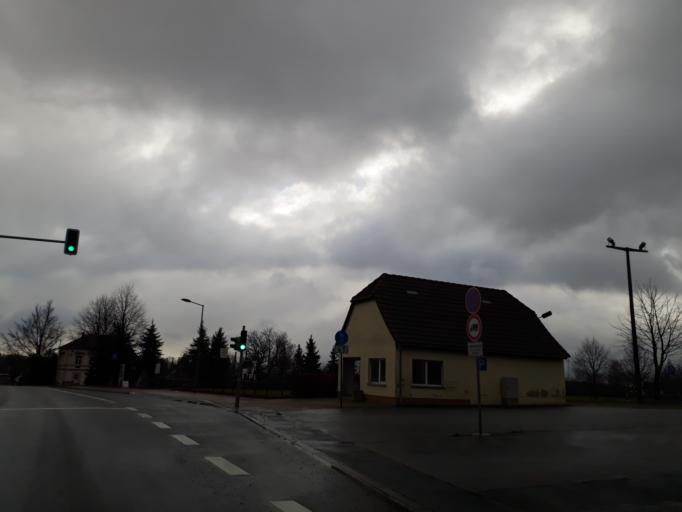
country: DE
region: Saxony
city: Herrnhut
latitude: 51.0296
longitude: 14.7214
